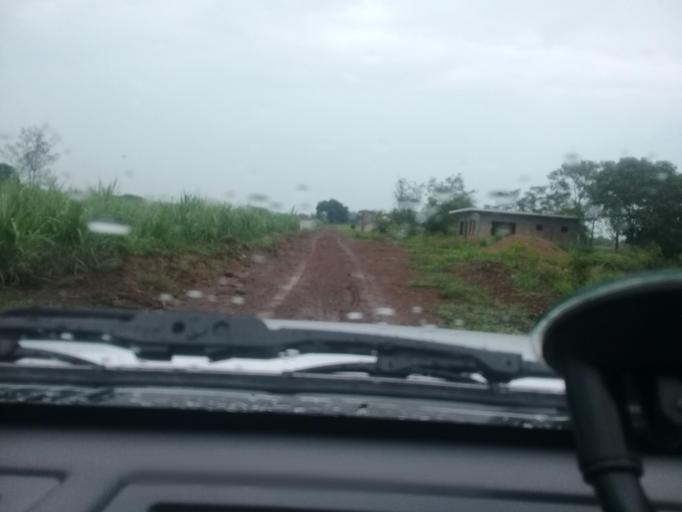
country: MX
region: Veracruz
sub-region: Puente Nacional
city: Cabezas
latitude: 19.3642
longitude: -96.3889
